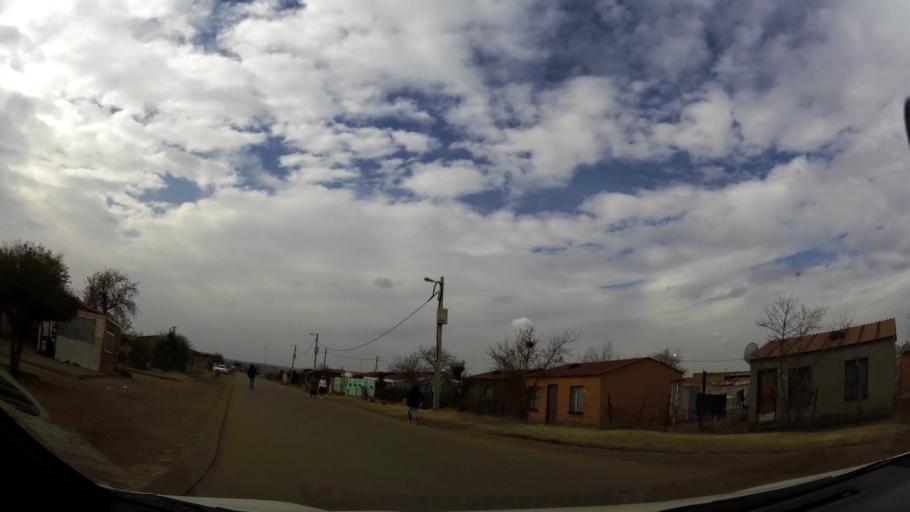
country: ZA
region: Gauteng
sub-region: Ekurhuleni Metropolitan Municipality
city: Germiston
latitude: -26.3966
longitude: 28.1553
